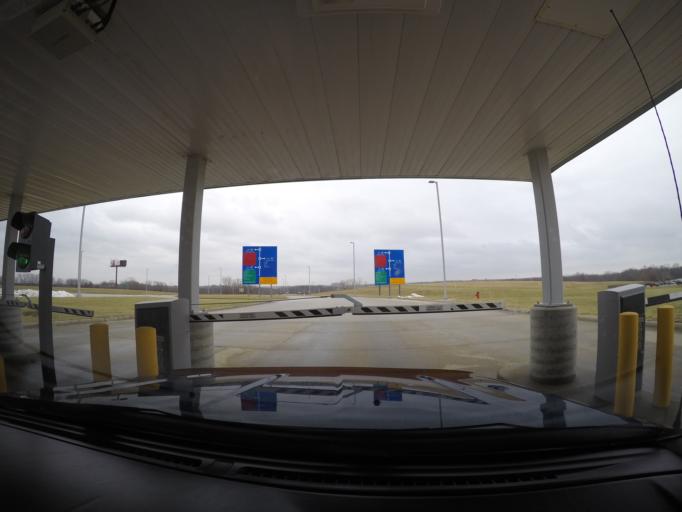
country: US
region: Missouri
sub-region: Platte County
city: Platte City
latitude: 39.3249
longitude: -94.7098
